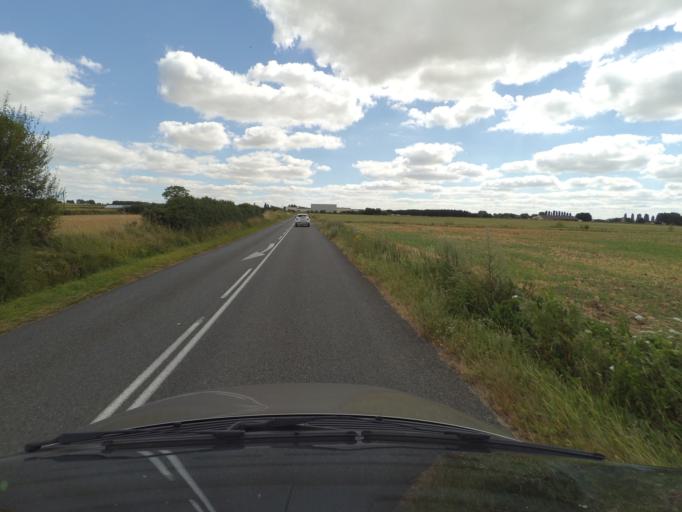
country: FR
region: Pays de la Loire
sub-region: Departement de Maine-et-Loire
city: Doue-la-Fontaine
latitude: 47.2087
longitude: -0.2770
